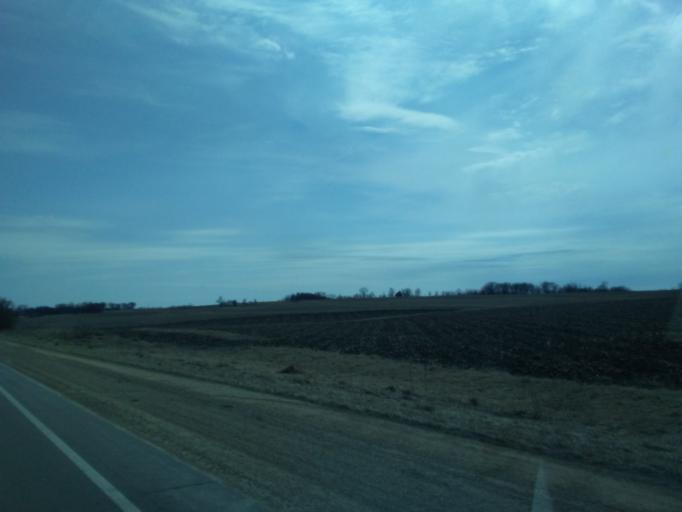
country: US
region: Iowa
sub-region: Winneshiek County
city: Decorah
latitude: 43.4096
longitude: -91.8562
